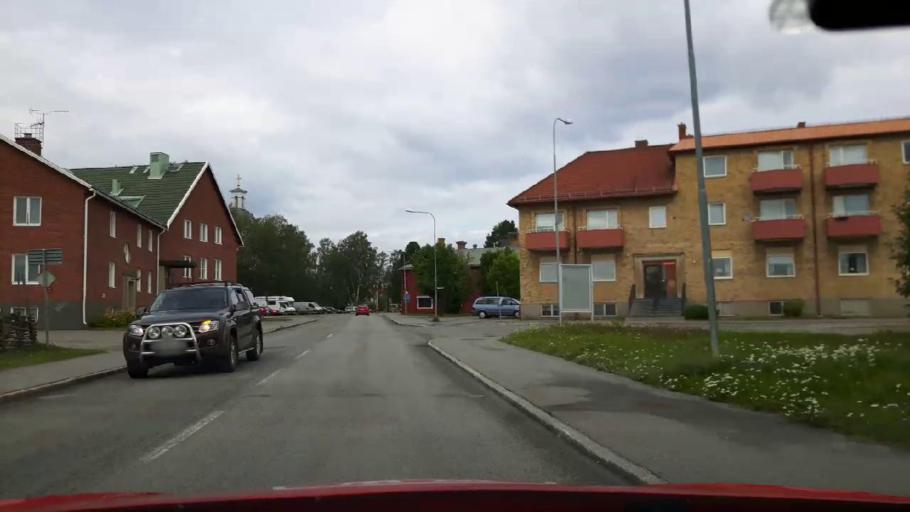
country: SE
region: Jaemtland
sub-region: Stroemsunds Kommun
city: Stroemsund
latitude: 63.8505
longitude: 15.5582
